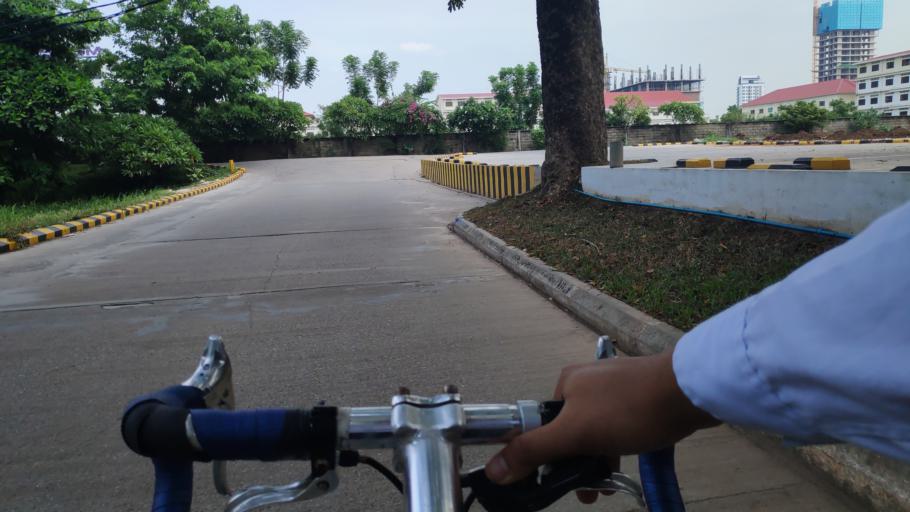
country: KH
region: Phnom Penh
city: Phnom Penh
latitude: 11.5699
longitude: 104.8968
